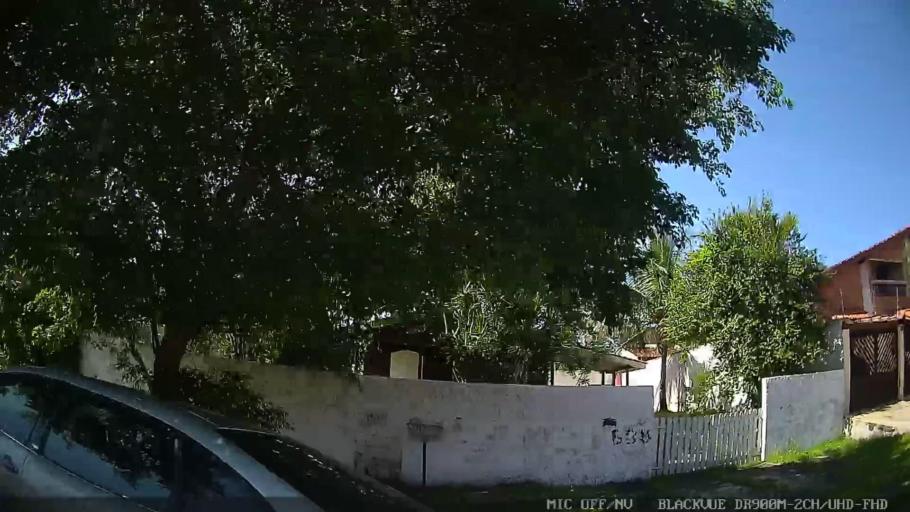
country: BR
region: Sao Paulo
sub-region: Peruibe
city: Peruibe
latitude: -24.3129
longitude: -46.9957
